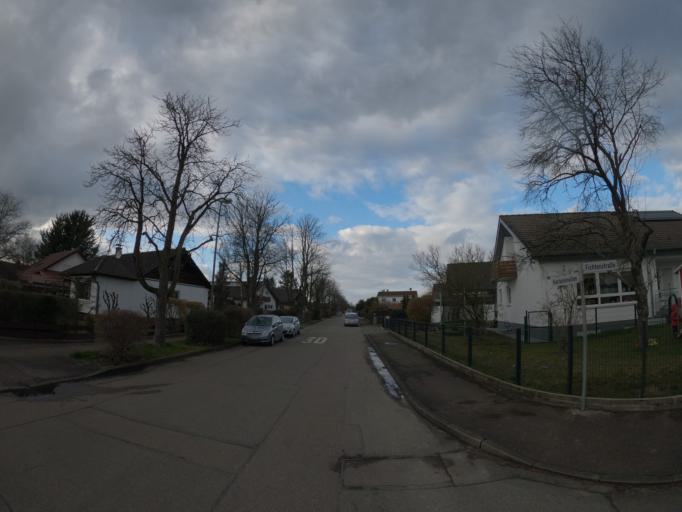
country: DE
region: Baden-Wuerttemberg
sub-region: Regierungsbezirk Stuttgart
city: Heiningen
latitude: 48.6574
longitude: 9.6406
